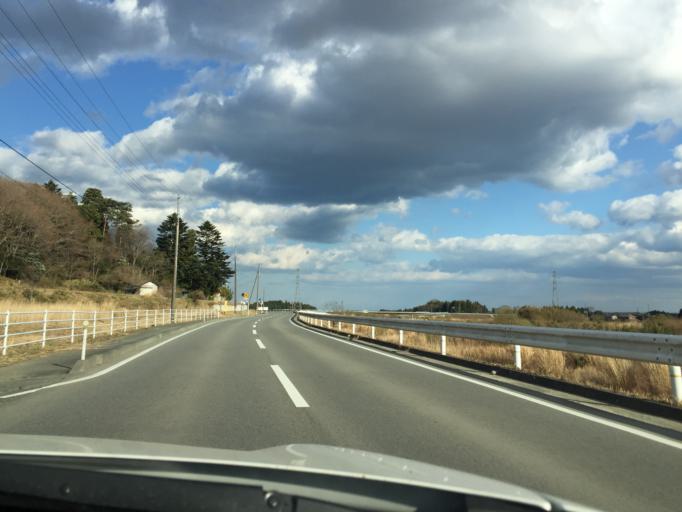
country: JP
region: Fukushima
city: Namie
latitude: 37.4135
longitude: 140.9559
